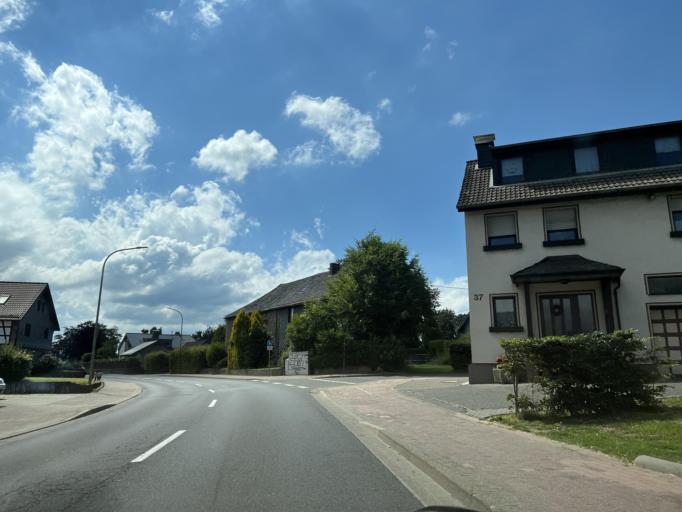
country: DE
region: North Rhine-Westphalia
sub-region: Regierungsbezirk Koln
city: Simmerath
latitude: 50.6075
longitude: 6.3229
